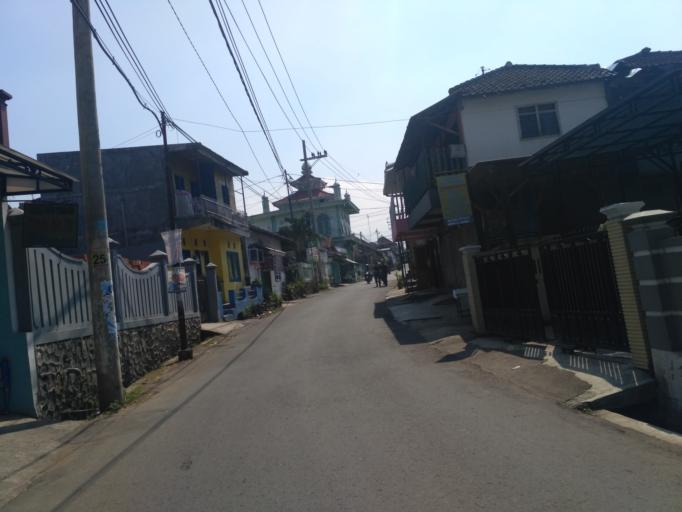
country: ID
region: East Java
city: Batu
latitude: -7.9037
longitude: 112.5812
